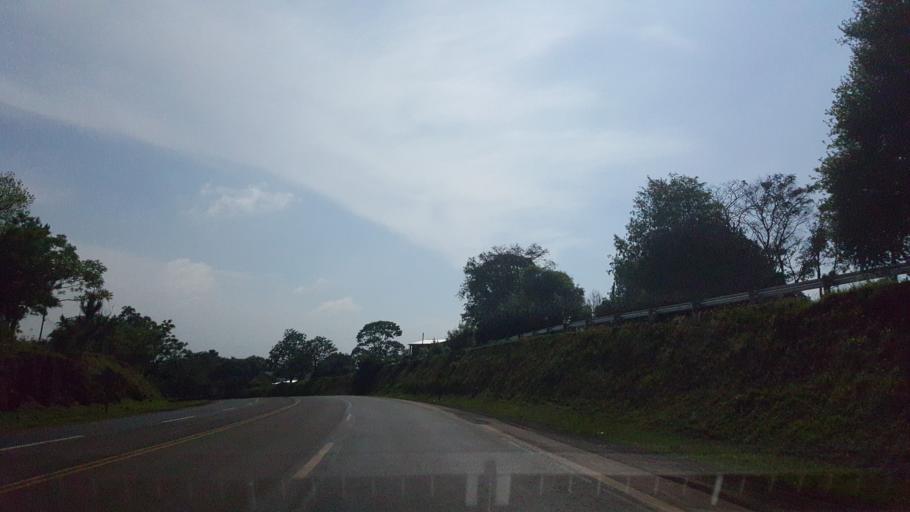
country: AR
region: Misiones
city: Capiovi
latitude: -26.9342
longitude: -55.0613
